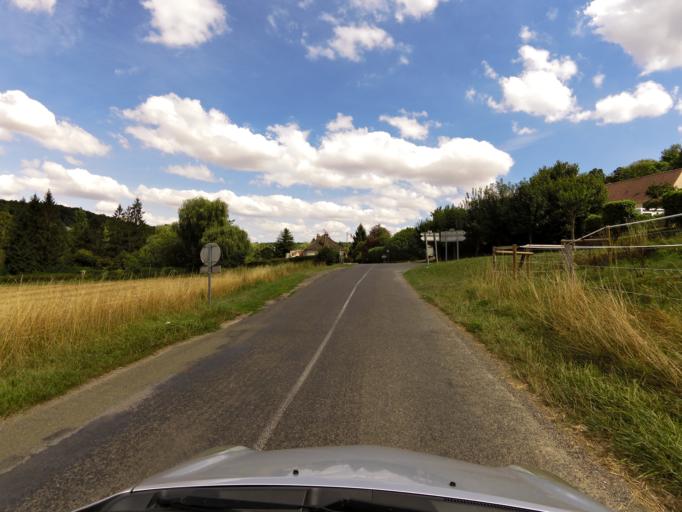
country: FR
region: Picardie
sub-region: Departement de l'Aisne
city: Neuilly-Saint-Front
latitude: 49.2520
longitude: 3.2058
